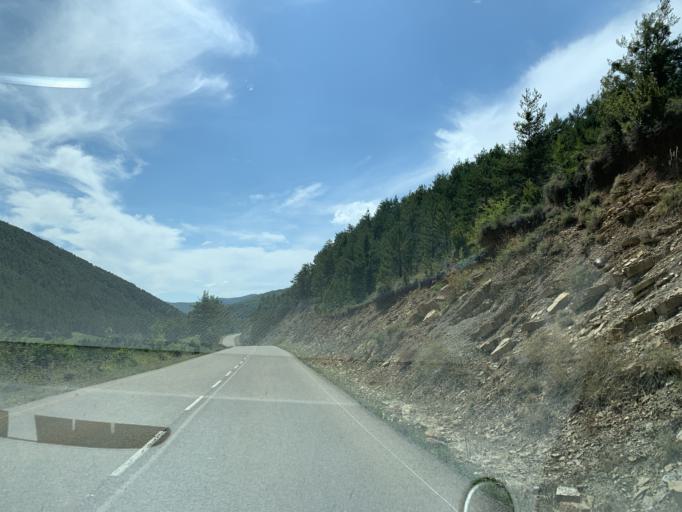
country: ES
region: Aragon
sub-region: Provincia de Huesca
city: Borau
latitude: 42.6514
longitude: -0.6370
